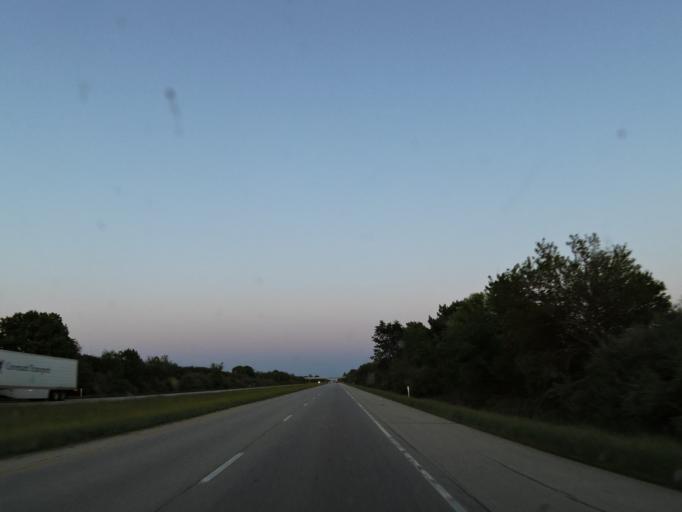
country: US
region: Indiana
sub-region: Montgomery County
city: Crawfordsville
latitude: 39.9957
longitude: -86.7213
